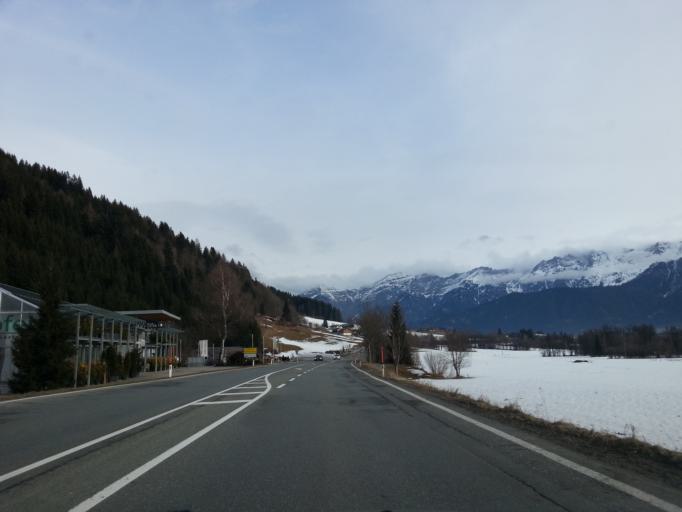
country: AT
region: Salzburg
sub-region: Politischer Bezirk Zell am See
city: Maishofen
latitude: 47.4058
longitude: 12.8085
